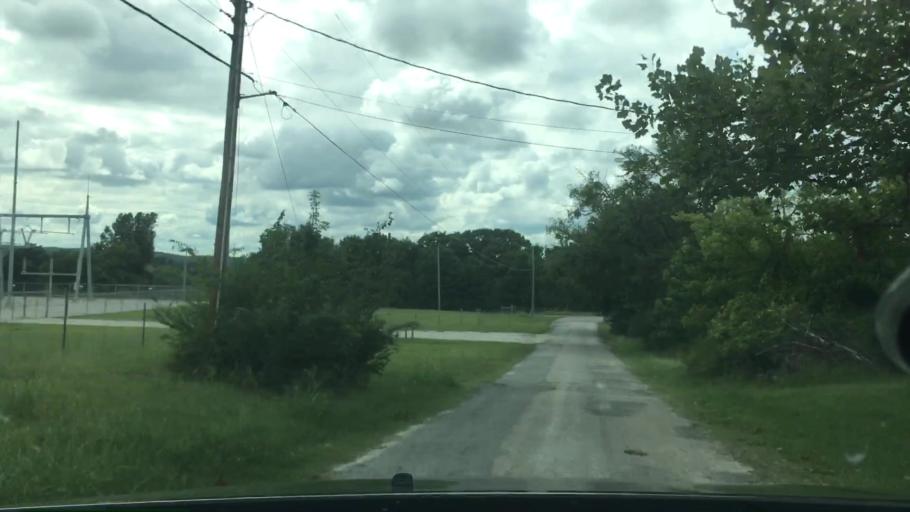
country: US
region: Oklahoma
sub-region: Pontotoc County
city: Ada
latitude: 34.7526
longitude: -96.6510
